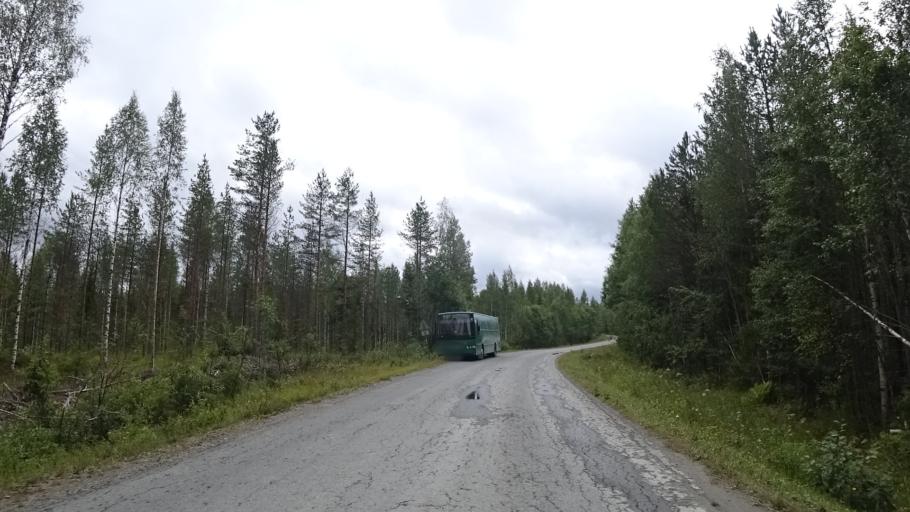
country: FI
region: North Karelia
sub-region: Joensuu
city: Ilomantsi
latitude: 62.9942
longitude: 31.2794
